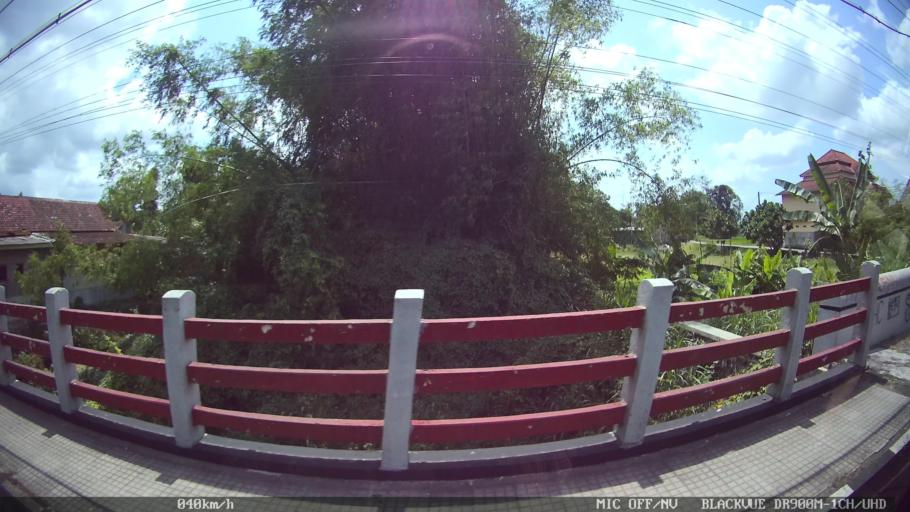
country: ID
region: Daerah Istimewa Yogyakarta
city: Bantul
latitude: -7.9089
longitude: 110.3482
